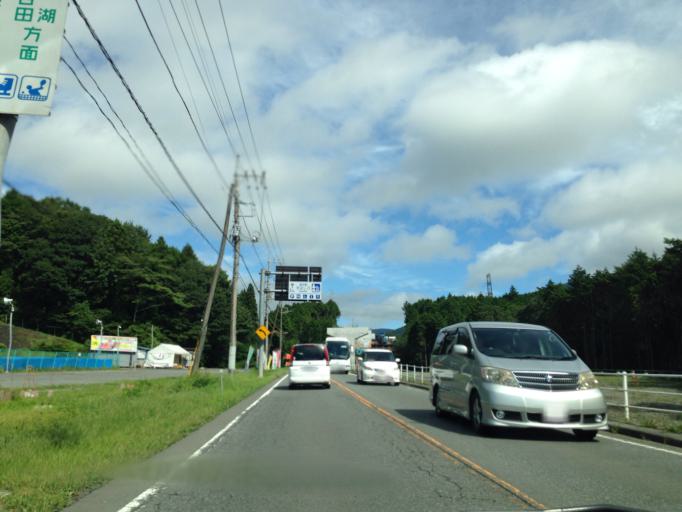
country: JP
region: Shizuoka
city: Gotemba
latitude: 35.3481
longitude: 138.8784
